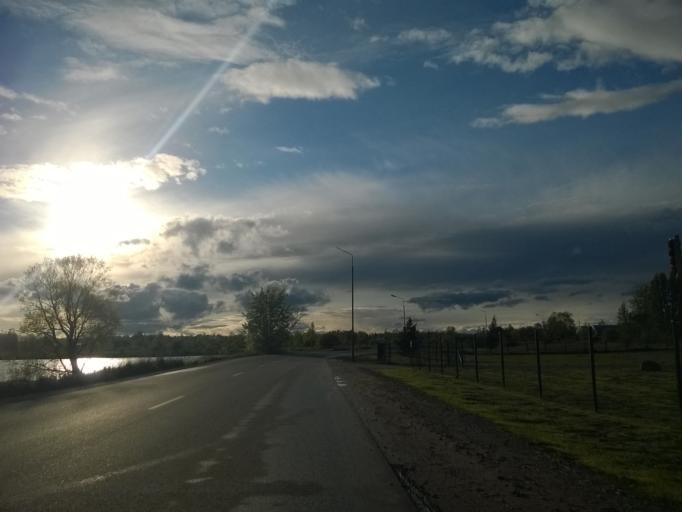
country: LV
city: Tireli
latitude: 56.9352
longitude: 23.6040
